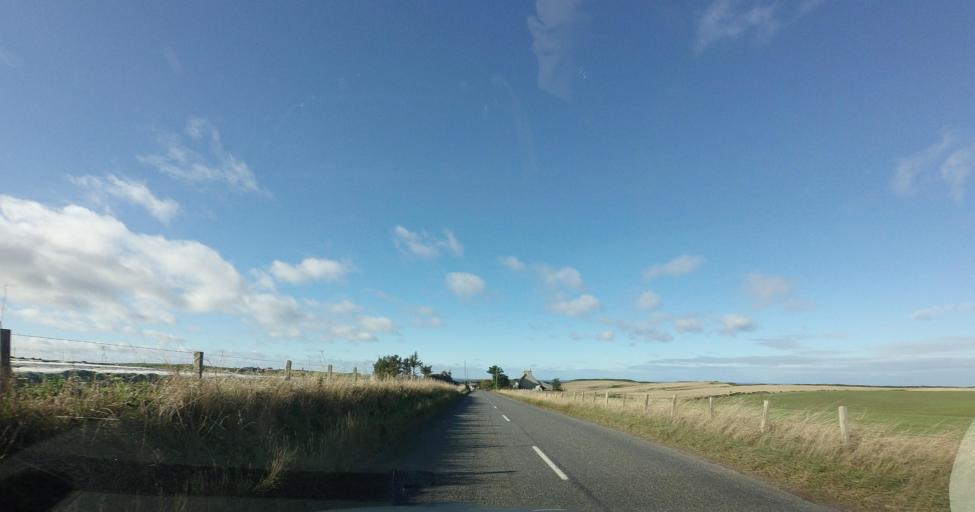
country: GB
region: Scotland
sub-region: Aberdeenshire
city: Macduff
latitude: 57.6635
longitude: -2.3804
